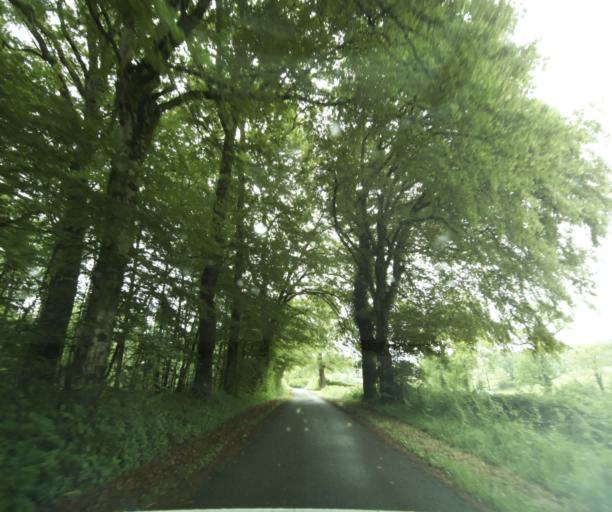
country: FR
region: Bourgogne
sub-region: Departement de Saone-et-Loire
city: Saint-Vallier
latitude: 46.4931
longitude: 4.4537
